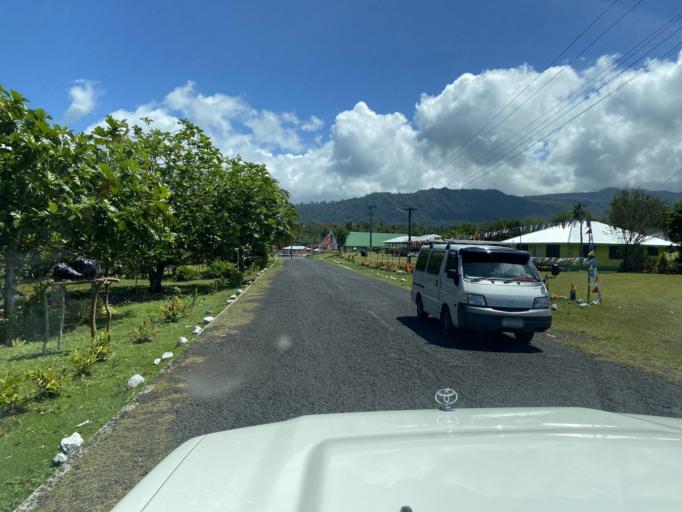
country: WS
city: Lotofaga
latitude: -13.9894
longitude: -171.8309
